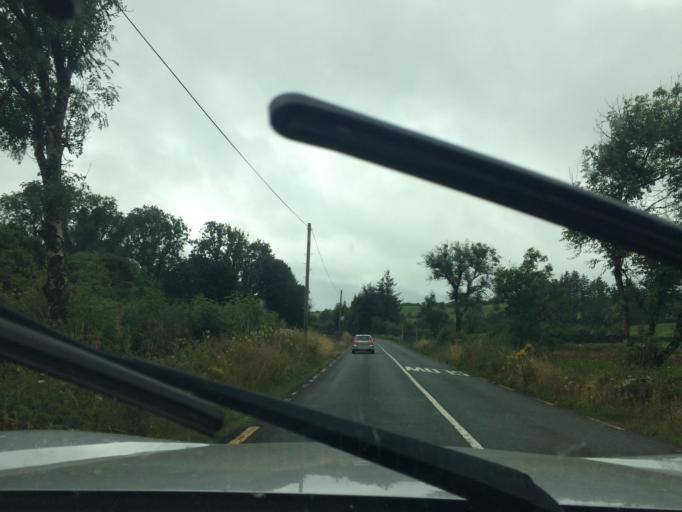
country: IE
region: Munster
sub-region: South Tipperary
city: Cluain Meala
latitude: 52.2465
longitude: -7.7199
